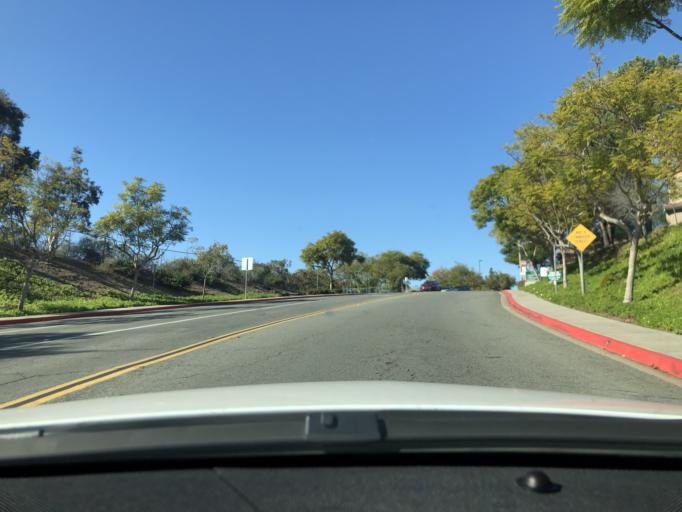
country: US
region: California
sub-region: San Diego County
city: Lemon Grove
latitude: 32.7384
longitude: -117.0585
